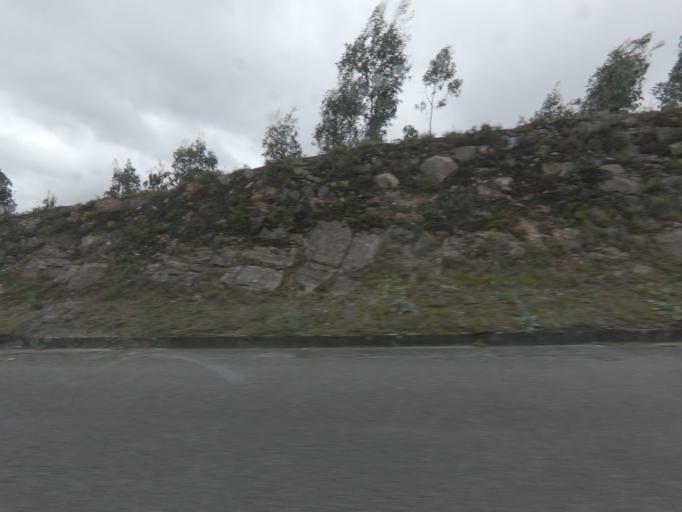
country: PT
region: Porto
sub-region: Paredes
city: Recarei
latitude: 41.1711
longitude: -8.4103
